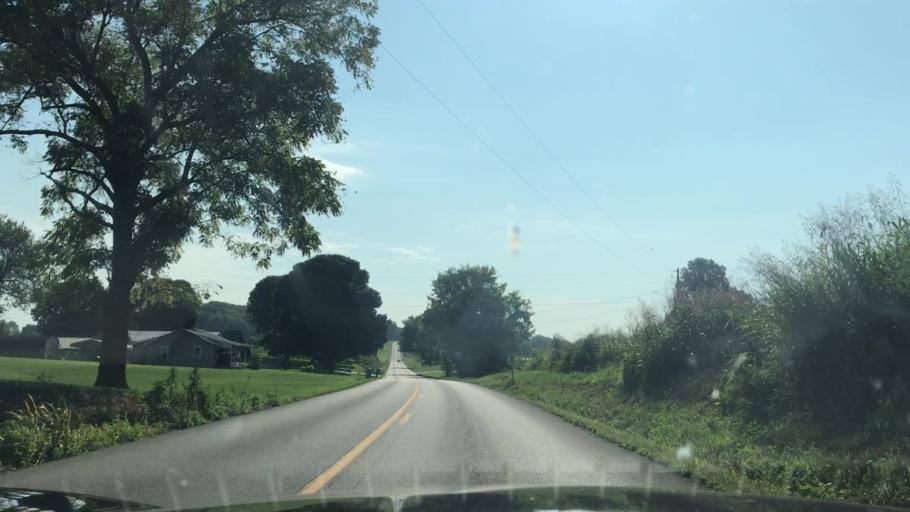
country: US
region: Kentucky
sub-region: Hart County
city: Horse Cave
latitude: 37.1664
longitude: -85.8308
